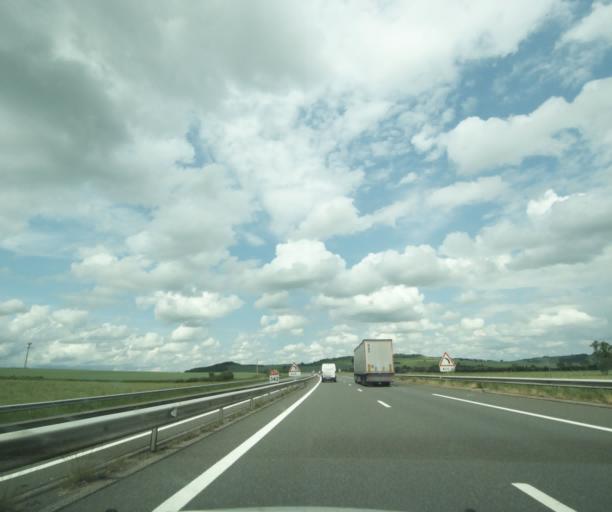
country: FR
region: Auvergne
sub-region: Departement de l'Allier
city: Ebreuil
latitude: 46.1603
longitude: 3.1268
